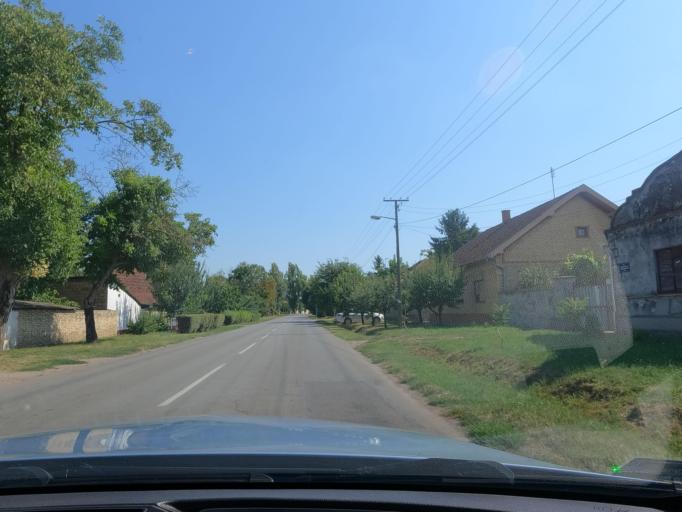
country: RS
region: Autonomna Pokrajina Vojvodina
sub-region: Severnobacki Okrug
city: Backa Topola
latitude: 45.8145
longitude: 19.6446
